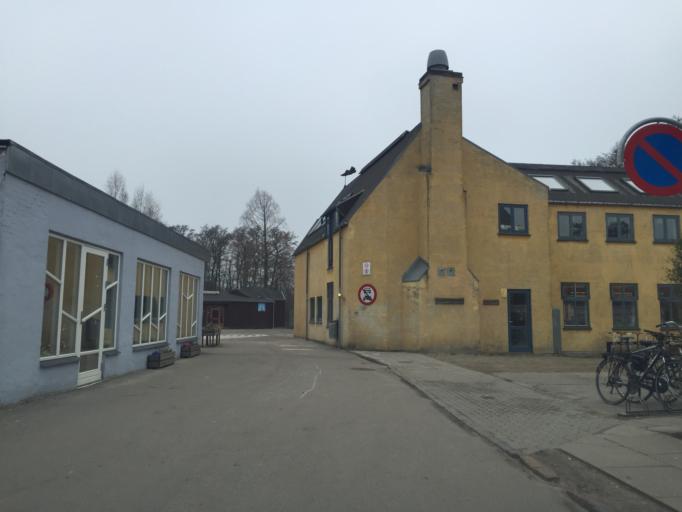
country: DK
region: Capital Region
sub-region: Lyngby-Tarbaek Kommune
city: Kongens Lyngby
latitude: 55.7540
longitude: 12.5316
